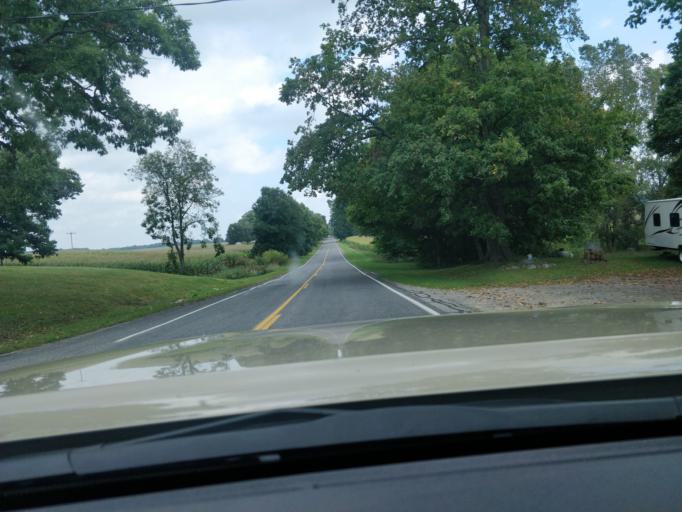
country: US
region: Michigan
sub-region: Ionia County
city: Saranac
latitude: 42.8861
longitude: -85.2774
